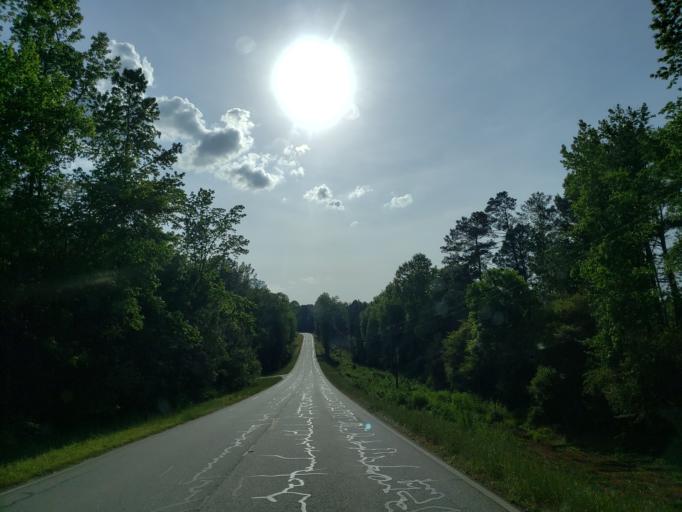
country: US
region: Georgia
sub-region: Carroll County
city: Bowdon
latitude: 33.4735
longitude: -85.2748
